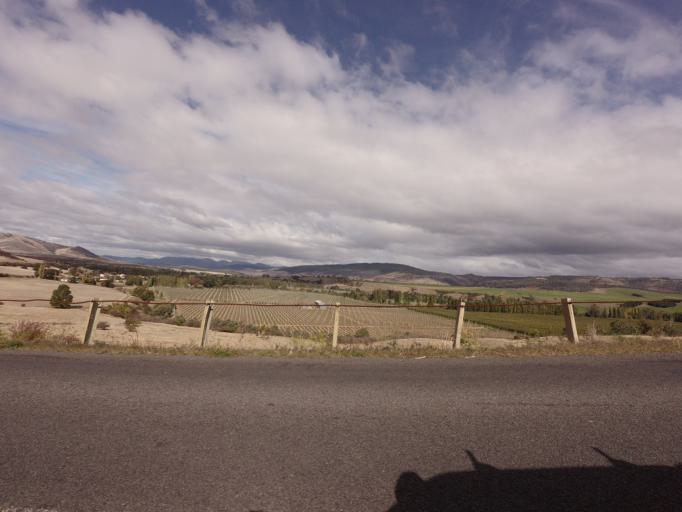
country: AU
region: Tasmania
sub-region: Derwent Valley
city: New Norfolk
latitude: -42.6915
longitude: 146.8790
